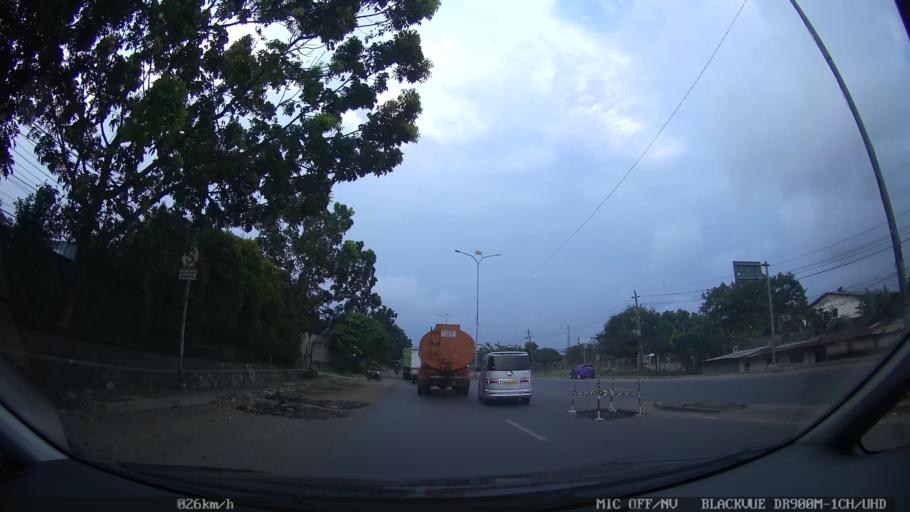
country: ID
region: Lampung
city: Bandarlampung
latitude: -5.4060
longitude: 105.2925
